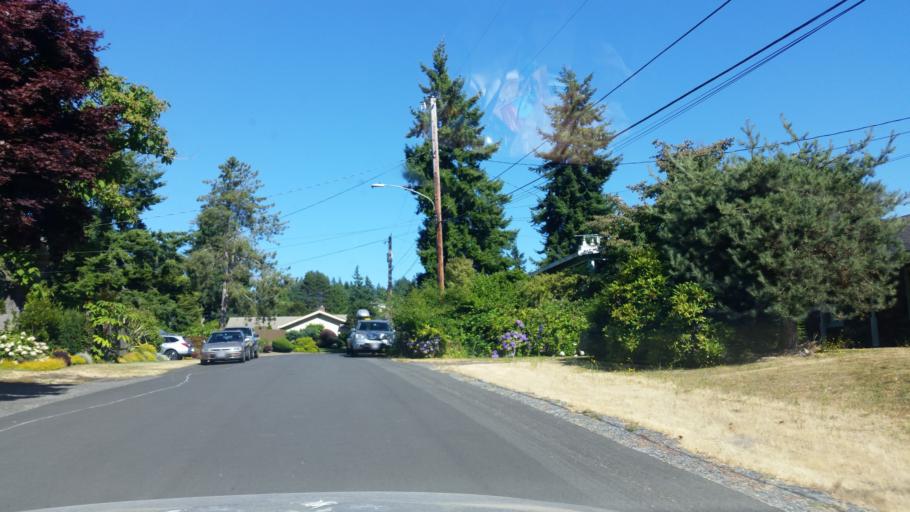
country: US
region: Washington
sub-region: Snohomish County
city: Edmonds
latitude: 47.8191
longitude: -122.3708
